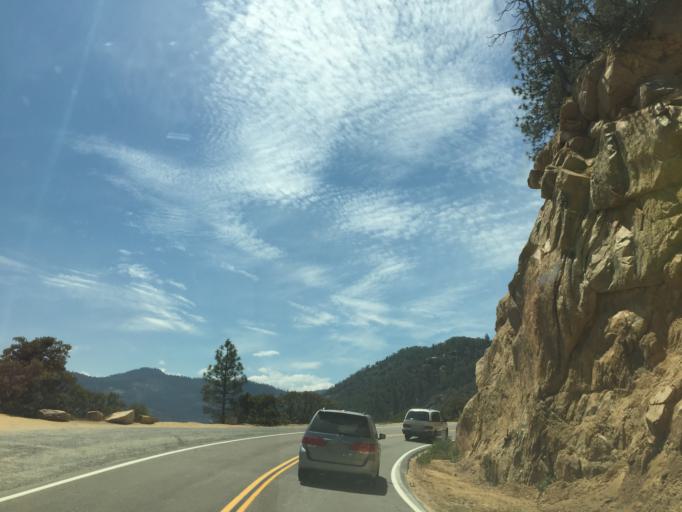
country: US
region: California
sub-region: Fresno County
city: Squaw Valley
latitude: 36.8169
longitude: -118.9087
